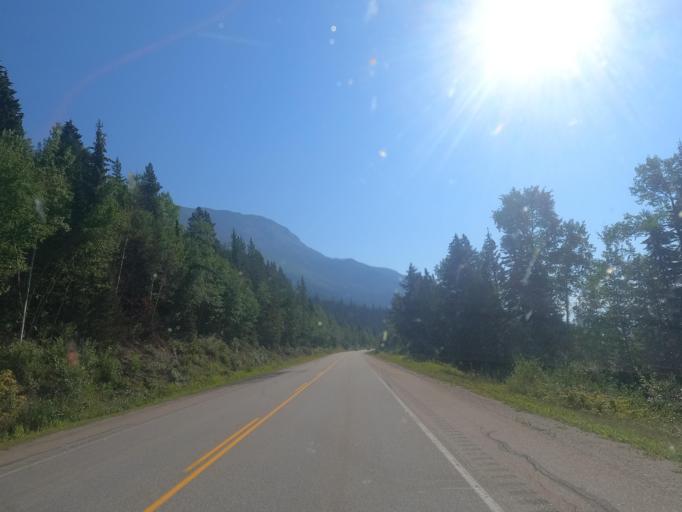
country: CA
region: Alberta
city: Jasper Park Lodge
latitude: 52.9725
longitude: -118.9448
